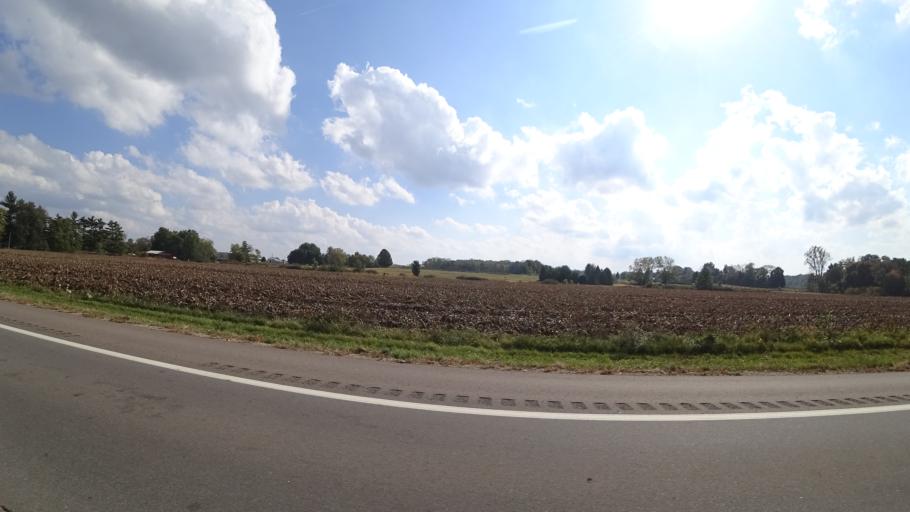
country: US
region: Michigan
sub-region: Calhoun County
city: Athens
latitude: 42.0597
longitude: -85.2180
